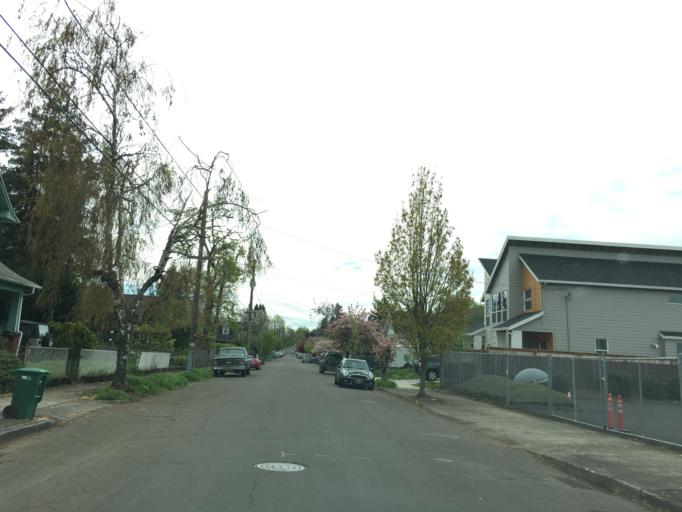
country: US
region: Oregon
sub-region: Multnomah County
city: Lents
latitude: 45.5260
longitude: -122.5859
